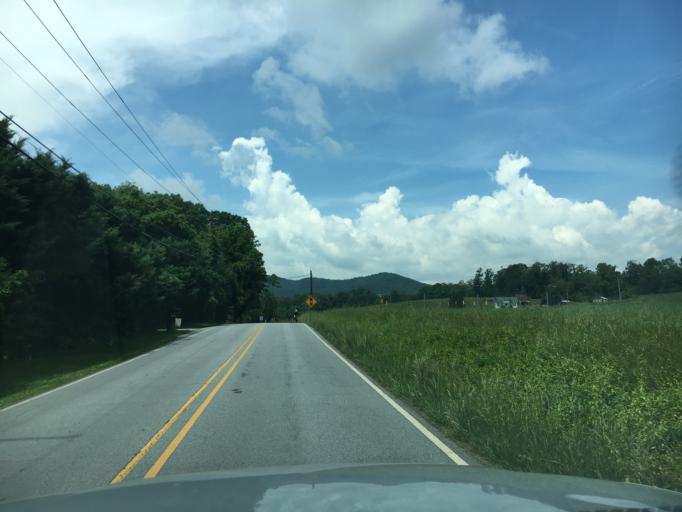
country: US
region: North Carolina
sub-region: Henderson County
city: Mills River
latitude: 35.3759
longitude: -82.5784
